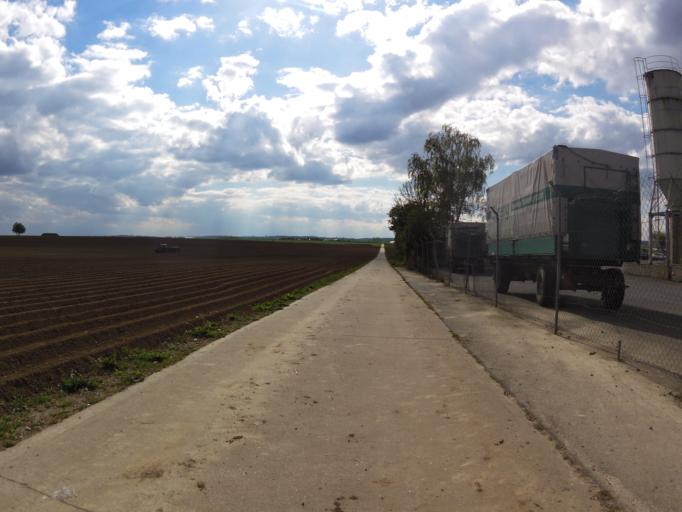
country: DE
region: Bavaria
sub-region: Regierungsbezirk Unterfranken
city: Oberpleichfeld
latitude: 49.8733
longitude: 10.0854
